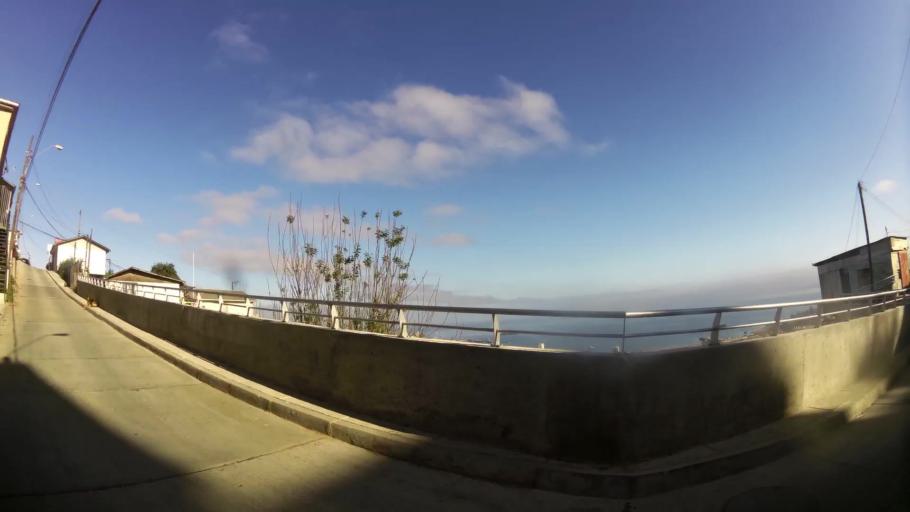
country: CL
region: Valparaiso
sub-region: Provincia de Valparaiso
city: Valparaiso
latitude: -33.0582
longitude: -71.6124
